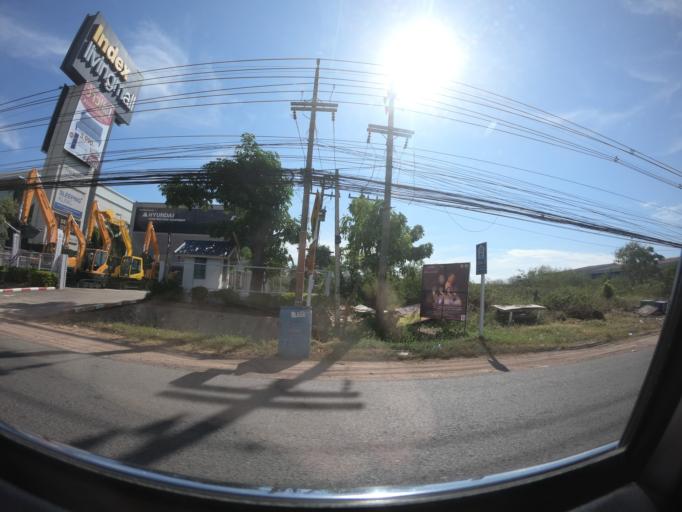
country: TH
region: Khon Kaen
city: Khon Kaen
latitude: 16.3971
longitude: 102.8139
